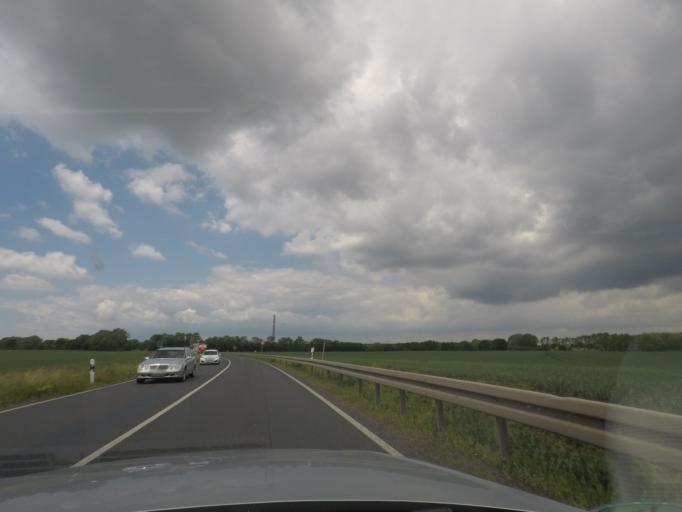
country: DE
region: Saxony
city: Markranstadt
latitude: 51.2814
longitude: 12.2543
